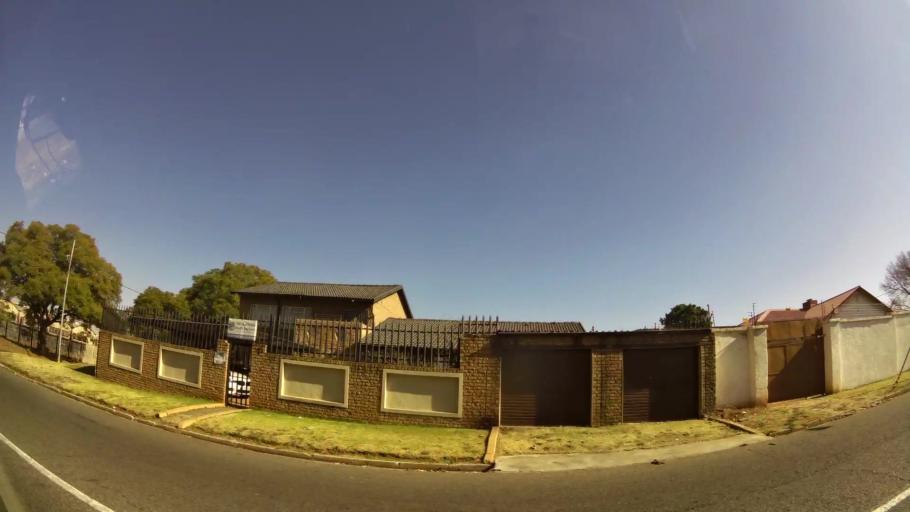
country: ZA
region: Gauteng
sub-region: City of Johannesburg Metropolitan Municipality
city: Johannesburg
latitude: -26.1976
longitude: 27.9853
